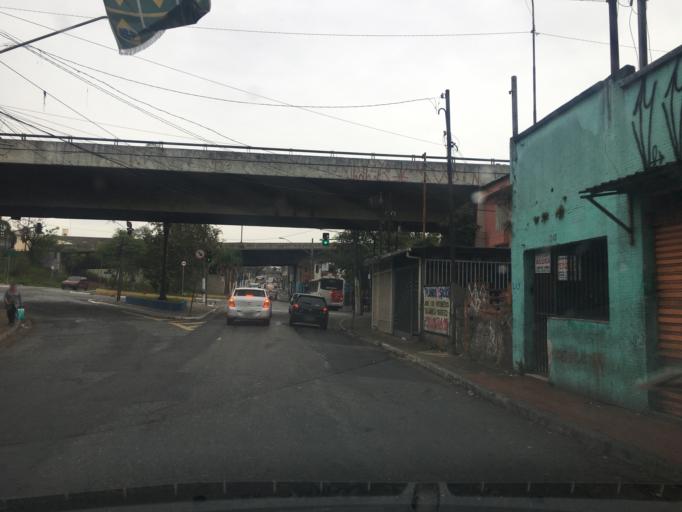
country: BR
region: Sao Paulo
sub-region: Guarulhos
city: Guarulhos
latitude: -23.5145
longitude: -46.5504
